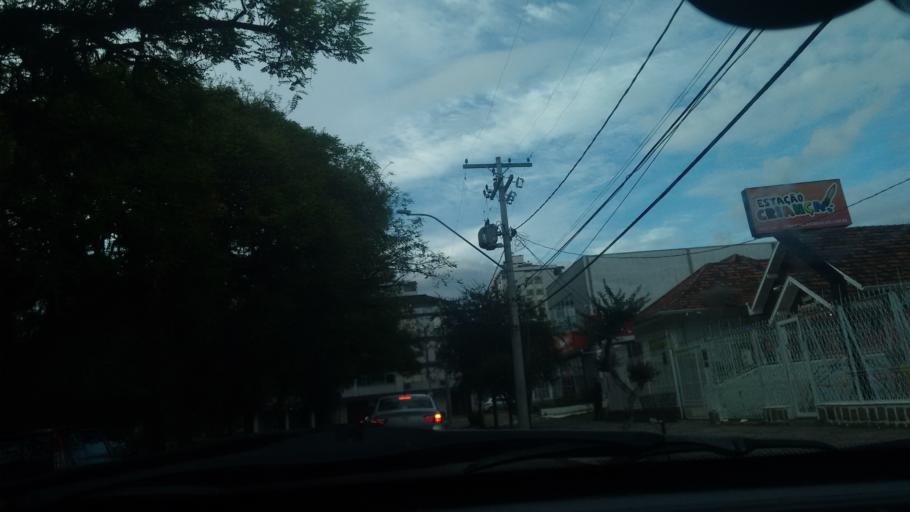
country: BR
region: Rio Grande do Sul
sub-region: Cachoeirinha
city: Cachoeirinha
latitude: -30.0054
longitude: -51.1518
